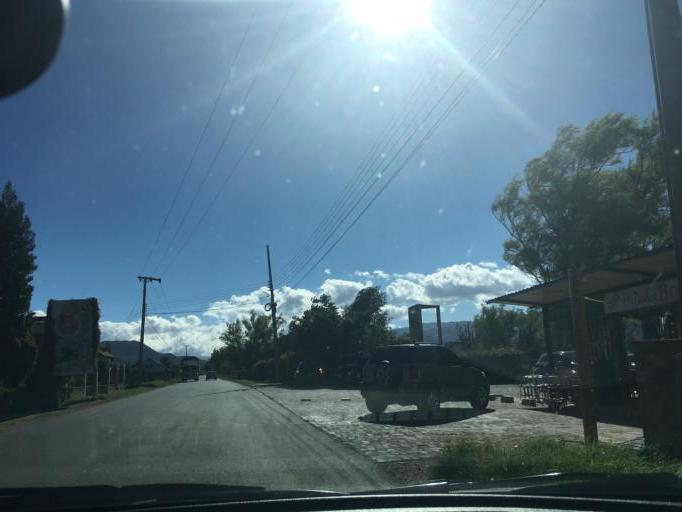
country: CO
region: Boyaca
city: Firavitoba
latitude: 5.6538
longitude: -72.9828
